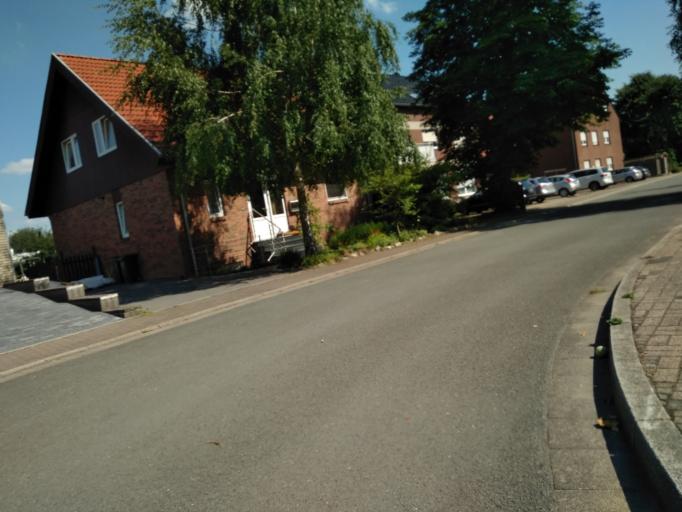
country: DE
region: North Rhine-Westphalia
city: Dorsten
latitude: 51.6801
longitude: 6.9498
